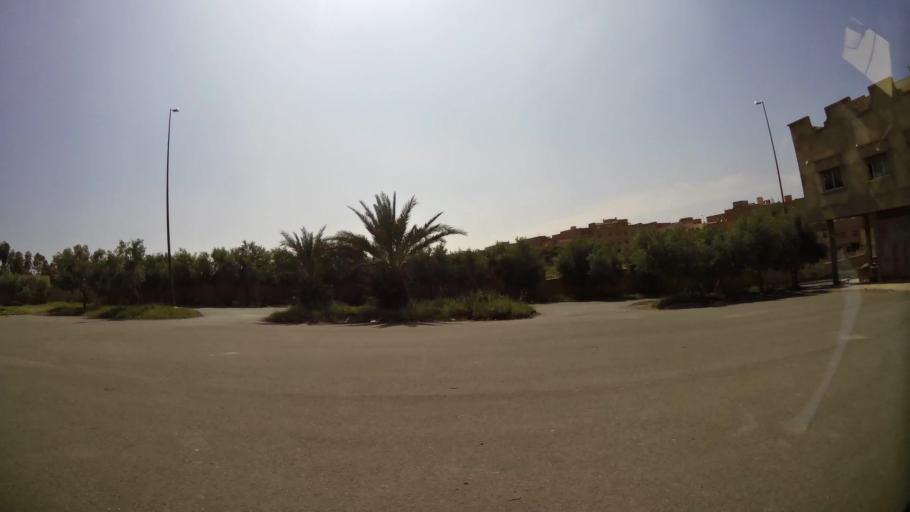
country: MA
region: Oriental
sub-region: Oujda-Angad
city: Oujda
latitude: 34.6900
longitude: -1.8735
